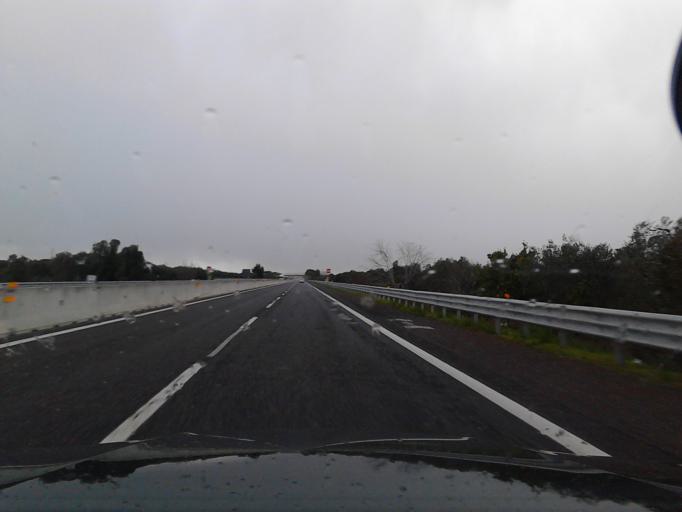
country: IT
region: Apulia
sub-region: Provincia di Bari
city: Bitonto
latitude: 41.1429
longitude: 16.6841
